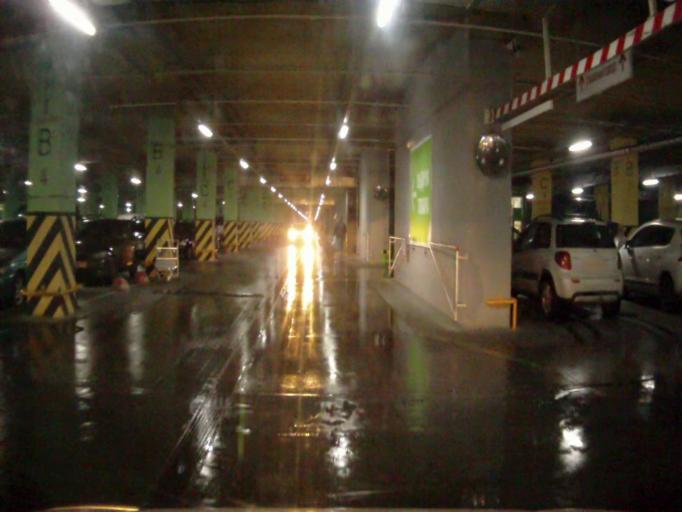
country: RU
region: Chelyabinsk
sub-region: Gorod Chelyabinsk
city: Chelyabinsk
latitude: 55.1464
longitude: 61.4489
